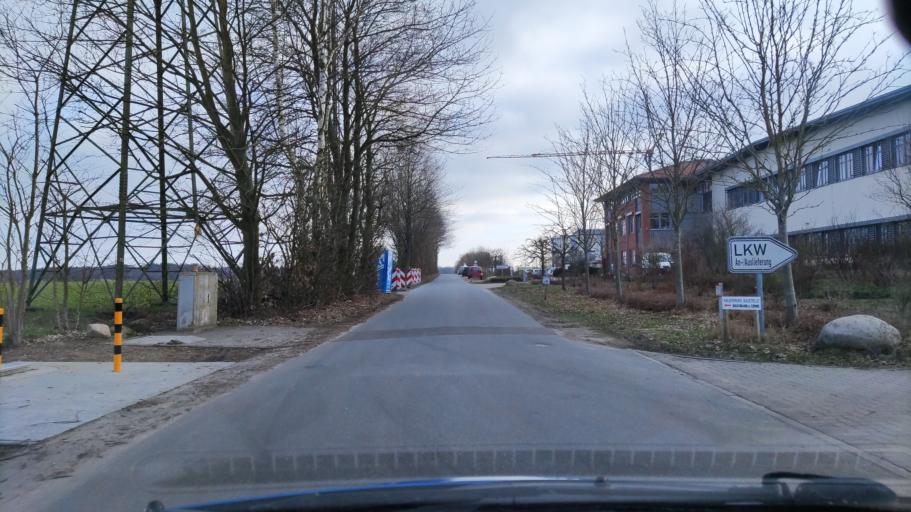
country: DE
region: Lower Saxony
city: Gerdau
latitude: 52.9598
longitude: 10.4523
